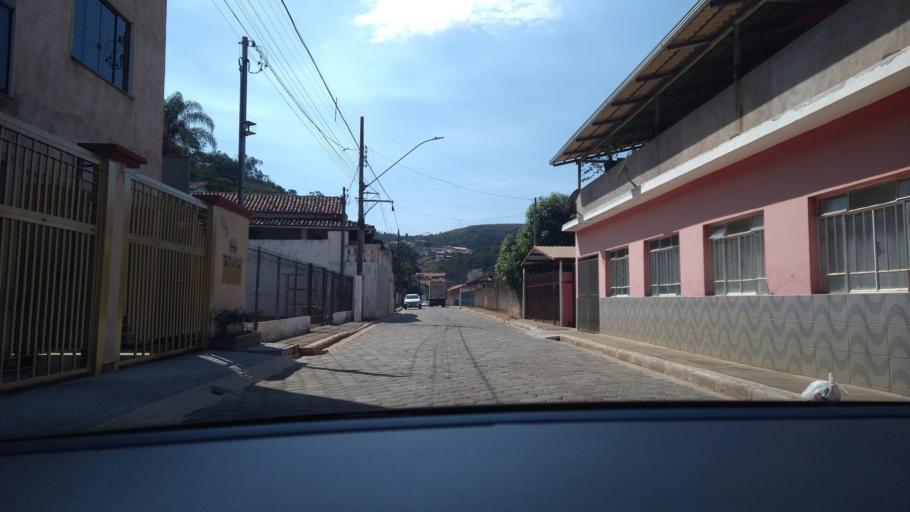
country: BR
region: Minas Gerais
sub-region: Rio Piracicaba
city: Rio Piracicaba
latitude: -19.9321
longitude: -43.1759
